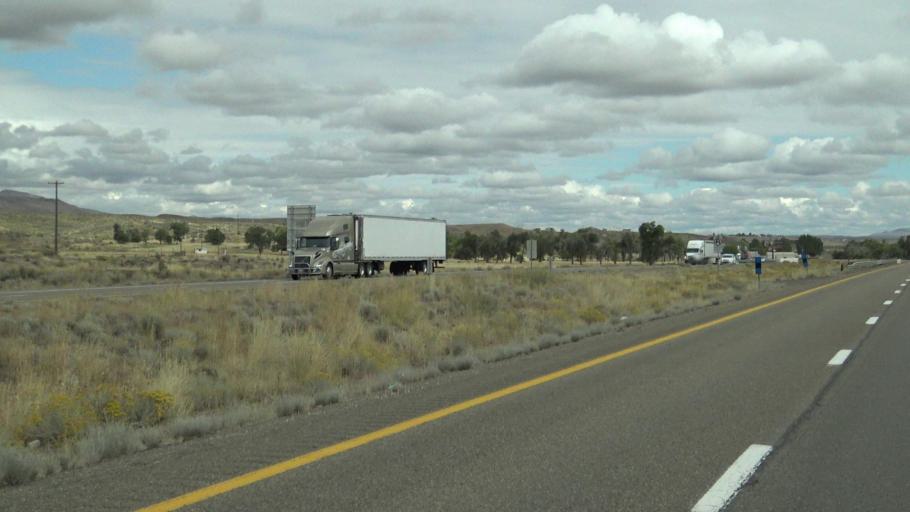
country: US
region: Nevada
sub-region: Elko County
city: Elko
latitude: 40.8777
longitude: -115.7199
